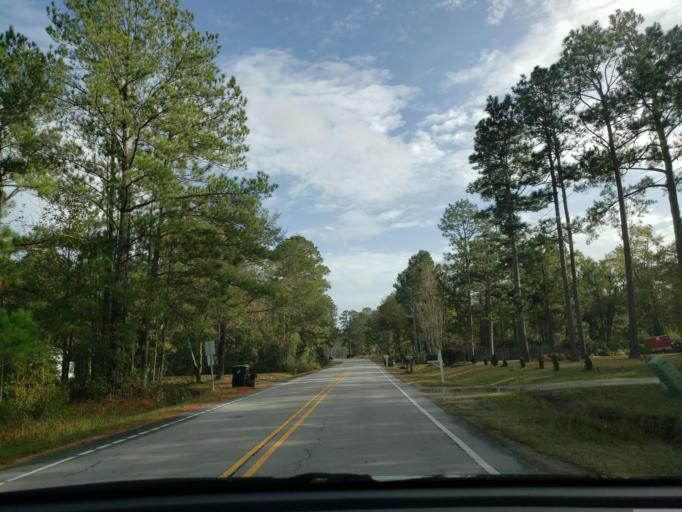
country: US
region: North Carolina
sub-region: Onslow County
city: Jacksonville
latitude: 34.6564
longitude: -77.4774
